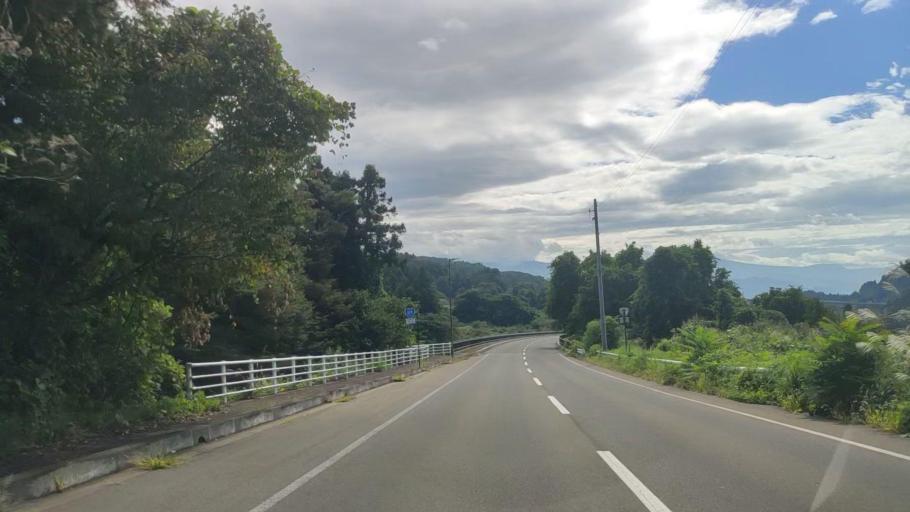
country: JP
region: Nagano
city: Nakano
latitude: 36.7917
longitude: 138.3166
